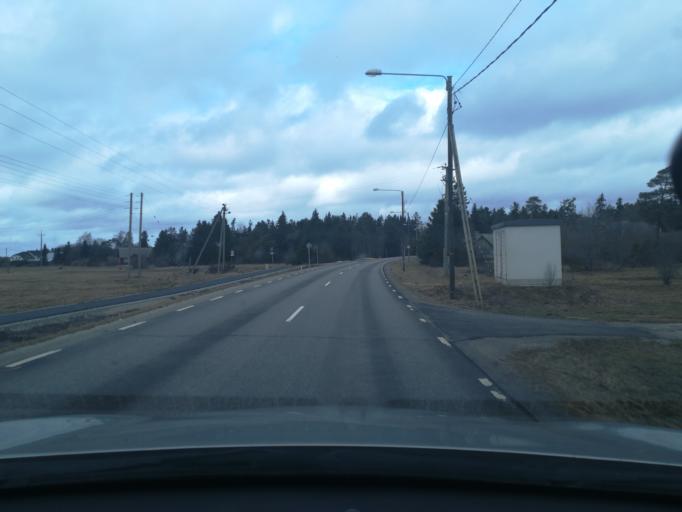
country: EE
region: Harju
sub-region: Harku vald
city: Tabasalu
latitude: 59.4321
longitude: 24.5197
